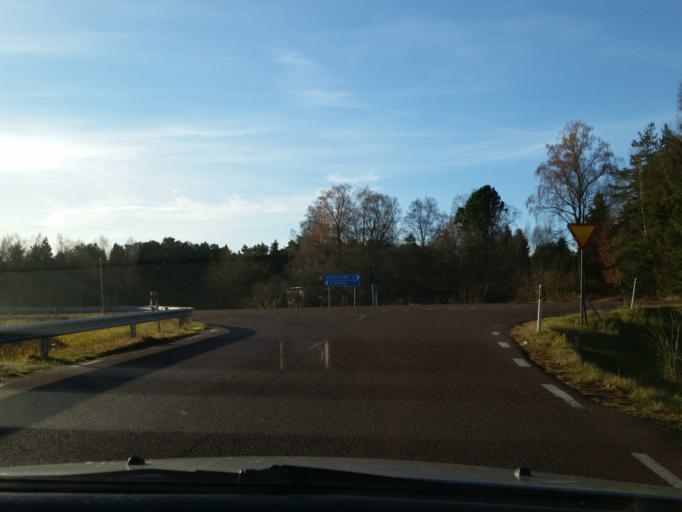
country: AX
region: Alands landsbygd
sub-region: Saltvik
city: Saltvik
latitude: 60.2411
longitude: 20.0644
